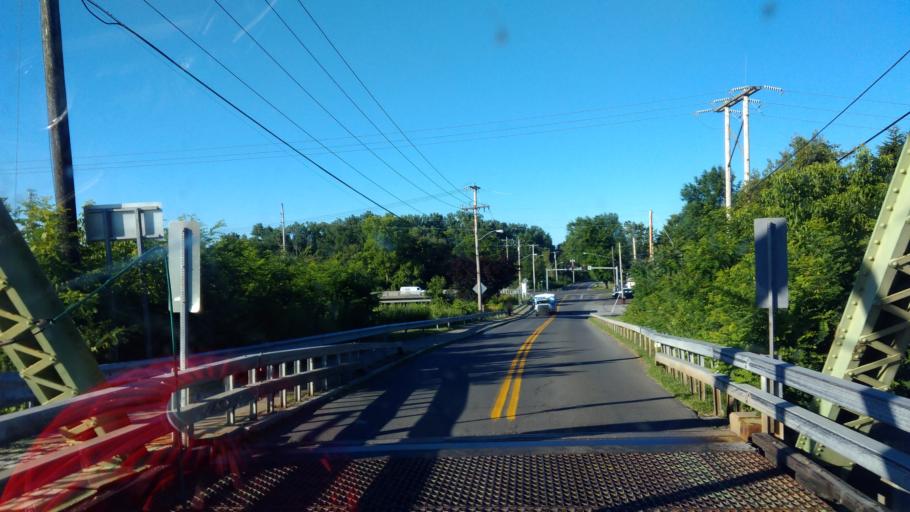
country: US
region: New York
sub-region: Wayne County
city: Lyons
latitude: 43.0619
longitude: -76.9966
